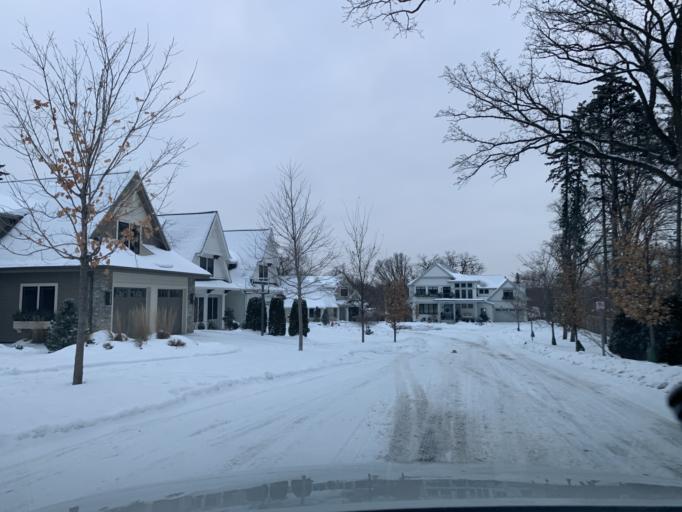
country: US
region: Minnesota
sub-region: Hennepin County
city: Saint Louis Park
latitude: 44.9237
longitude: -93.3386
